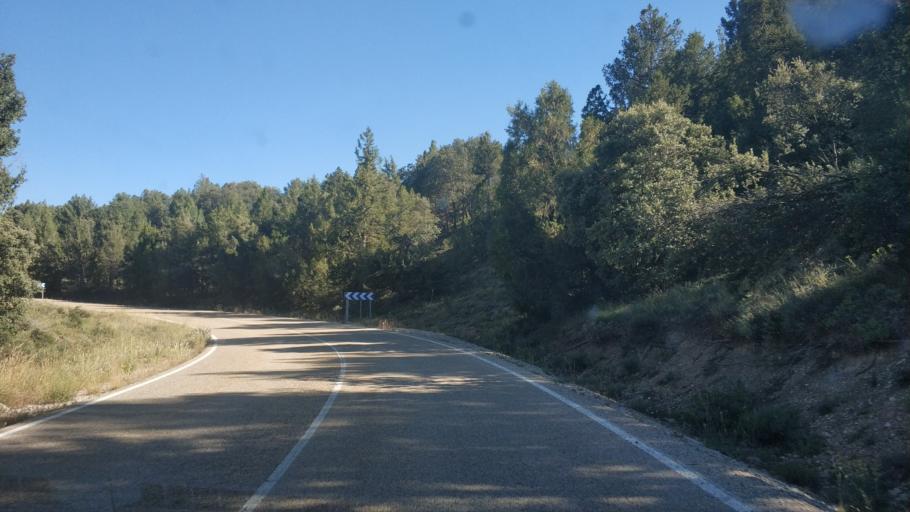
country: ES
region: Castille and Leon
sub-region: Provincia de Soria
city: Montejo de Tiermes
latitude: 41.4303
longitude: -3.2051
